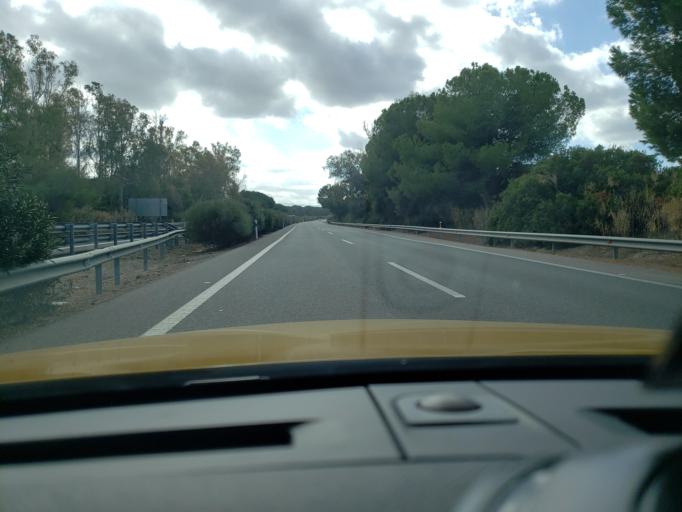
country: ES
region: Andalusia
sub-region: Provincia de Sevilla
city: Las Cabezas de San Juan
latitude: 36.9657
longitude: -5.9575
